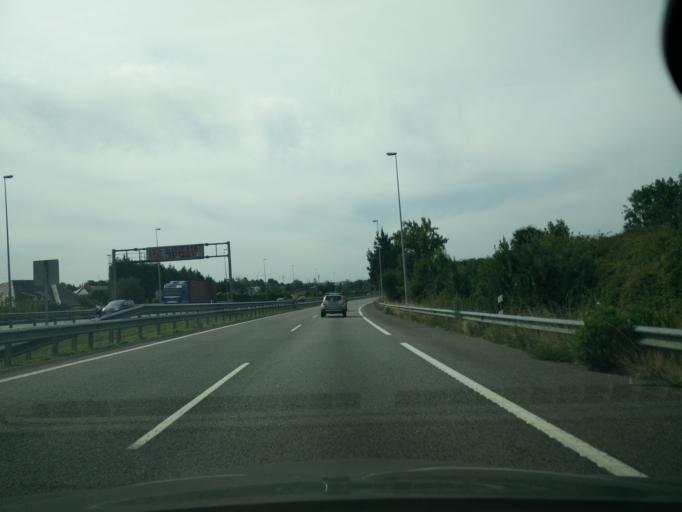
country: ES
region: Asturias
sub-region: Province of Asturias
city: Gijon
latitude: 43.5156
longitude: -5.6269
